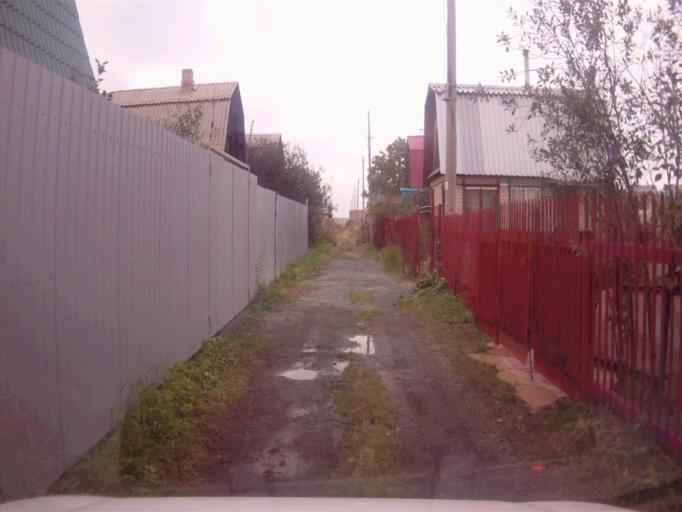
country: RU
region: Chelyabinsk
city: Novosineglazovskiy
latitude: 54.9830
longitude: 61.4047
